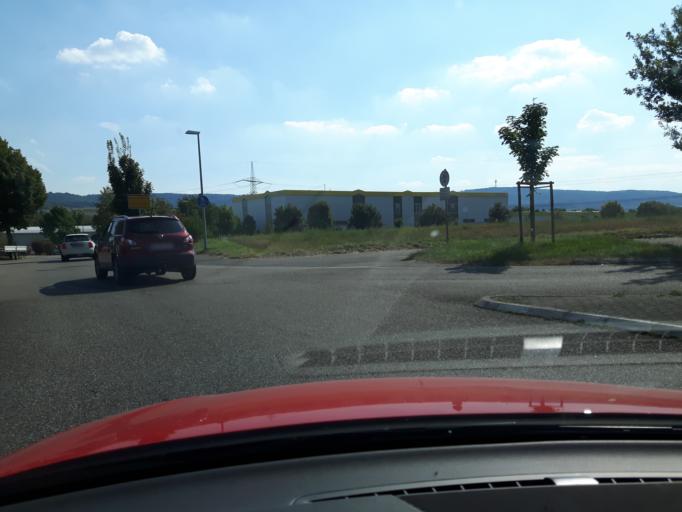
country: DE
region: Baden-Wuerttemberg
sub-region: Regierungsbezirk Stuttgart
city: Brackenheim
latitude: 49.0714
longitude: 9.0416
